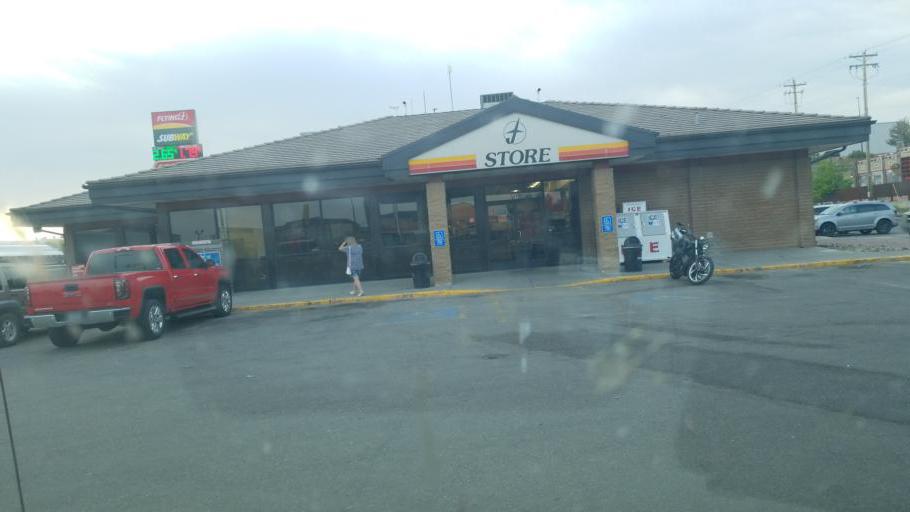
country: US
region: Wyoming
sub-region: Natrona County
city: Evansville
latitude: 42.8518
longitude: -106.2699
